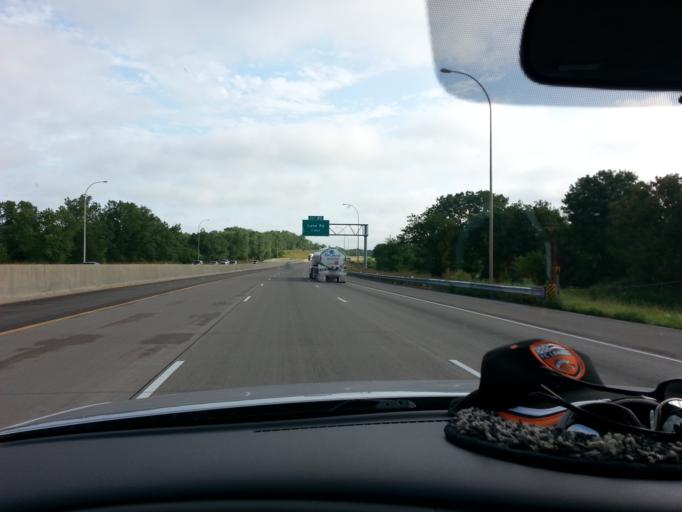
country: US
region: Minnesota
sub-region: Washington County
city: Newport
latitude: 44.8990
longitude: -92.9958
